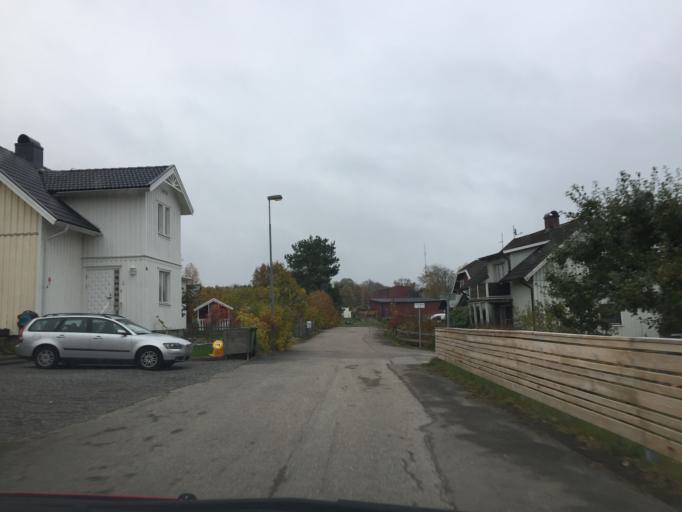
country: SE
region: Vaestra Goetaland
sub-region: Trollhattan
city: Sjuntorp
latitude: 58.1977
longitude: 12.2176
